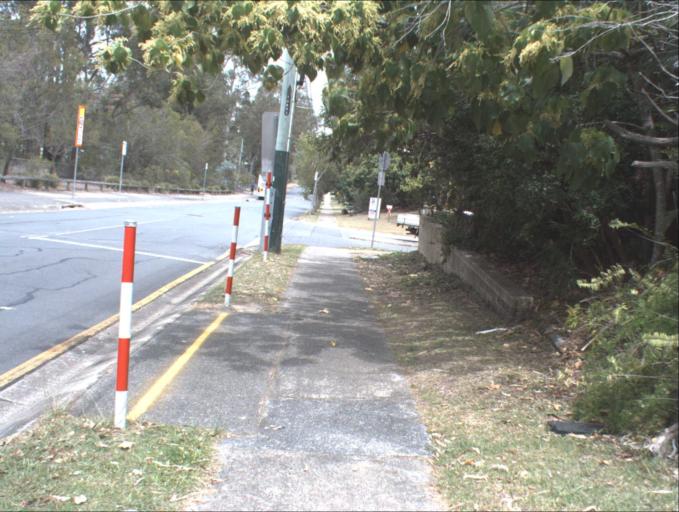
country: AU
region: Queensland
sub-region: Logan
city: Springwood
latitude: -27.6282
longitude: 153.1373
